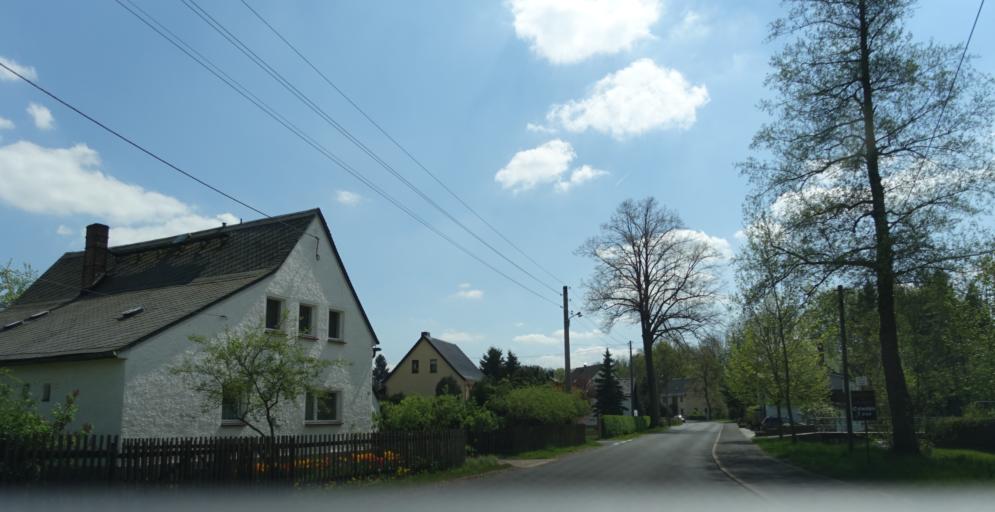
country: DE
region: Saxony
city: Oberschona
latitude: 50.8959
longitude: 13.2556
